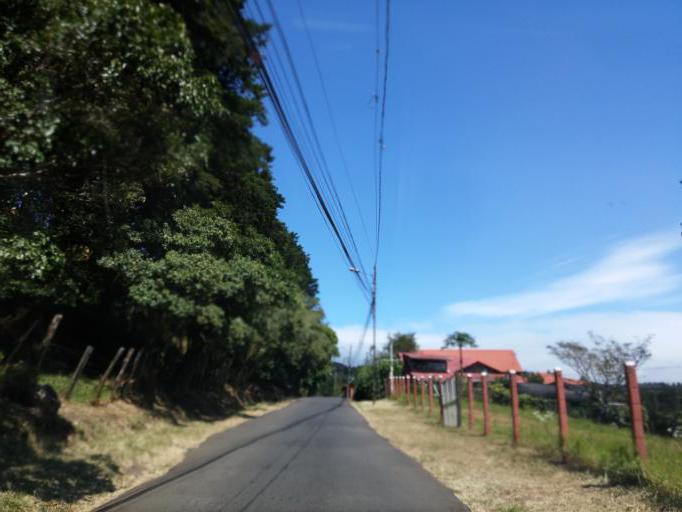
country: CR
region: Heredia
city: Santo Domingo
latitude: 10.0656
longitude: -84.1279
